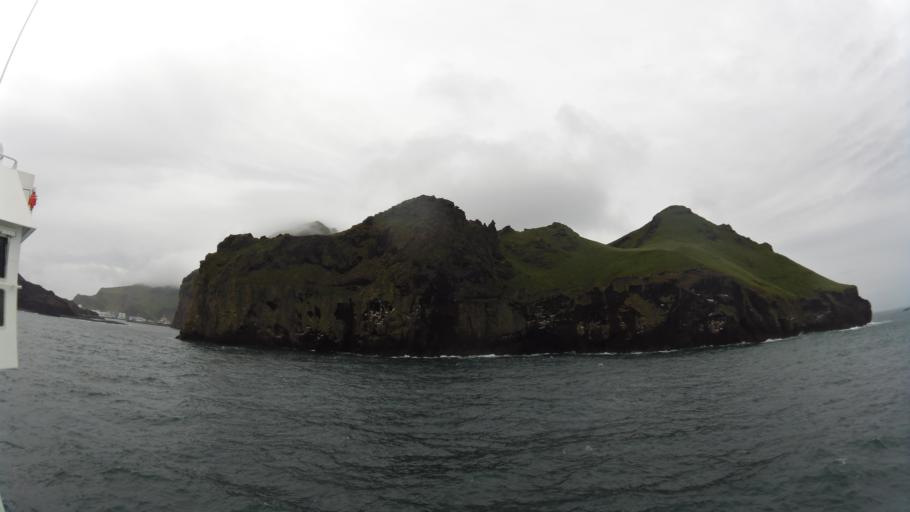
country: IS
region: South
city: Vestmannaeyjar
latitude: 63.4483
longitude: -20.2400
